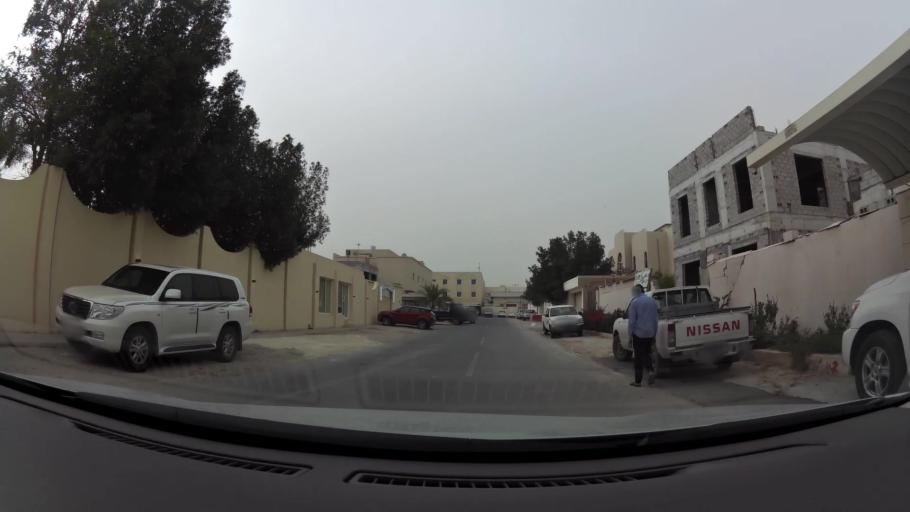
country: QA
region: Baladiyat ad Dawhah
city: Doha
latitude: 25.2592
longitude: 51.4925
